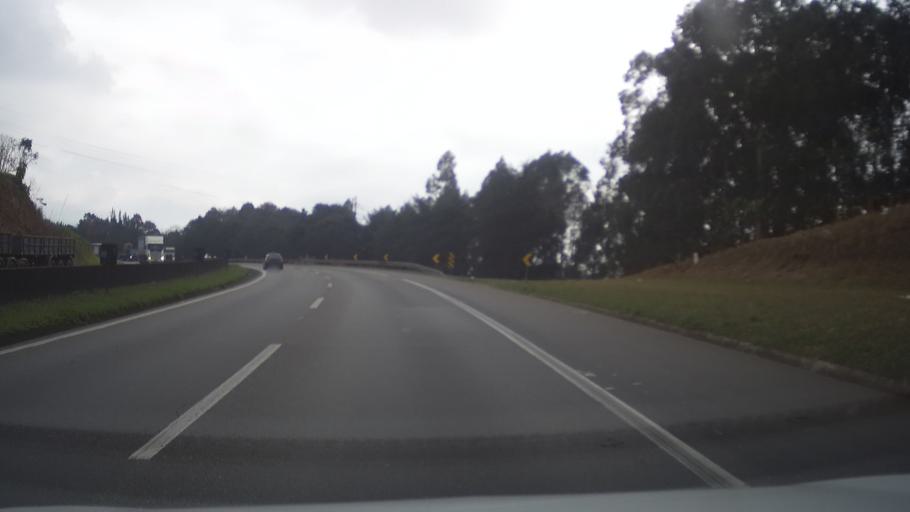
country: BR
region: Minas Gerais
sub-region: Extrema
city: Extrema
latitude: -22.8581
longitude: -46.3375
